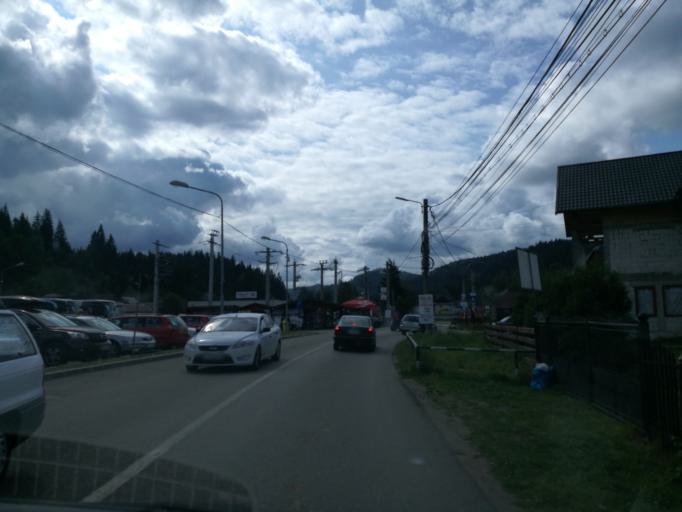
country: RO
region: Suceava
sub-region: Oras Gura Humorului
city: Gura Humorului
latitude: 47.5209
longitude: 25.8654
